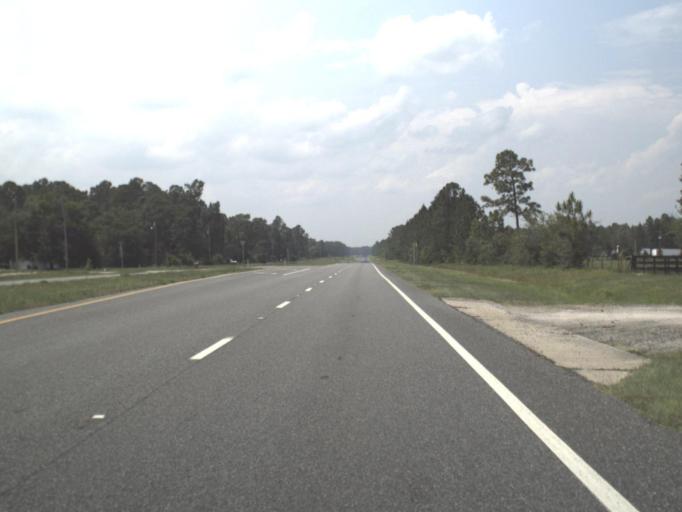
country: US
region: Florida
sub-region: Putnam County
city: East Palatka
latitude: 29.7855
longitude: -81.6456
